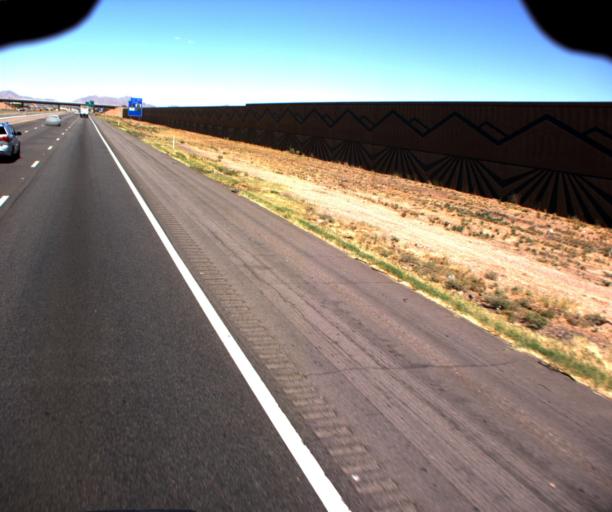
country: US
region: Arizona
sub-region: Pinal County
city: Casa Grande
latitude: 32.8610
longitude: -111.6869
